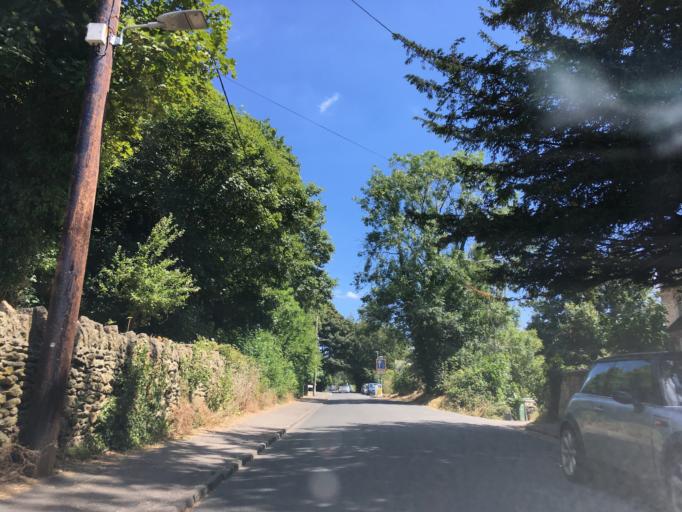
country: GB
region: England
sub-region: Gloucestershire
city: Stroud
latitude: 51.7424
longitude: -2.1998
